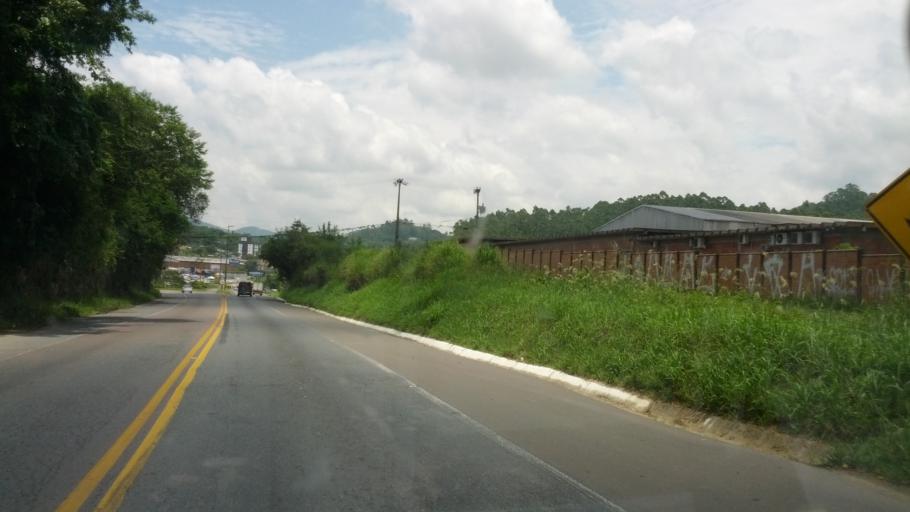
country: BR
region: Santa Catarina
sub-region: Blumenau
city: Blumenau
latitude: -26.8717
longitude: -49.1121
